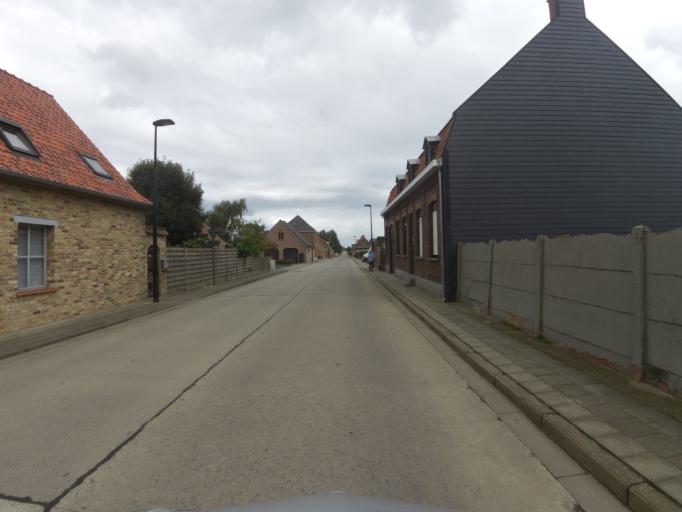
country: BE
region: Flanders
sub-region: Provincie West-Vlaanderen
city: Lichtervelde
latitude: 51.0381
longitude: 3.2064
